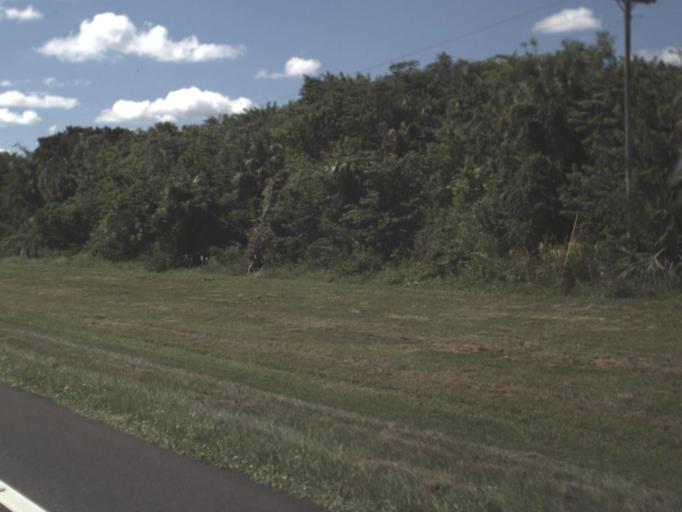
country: US
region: Florida
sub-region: Glades County
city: Buckhead Ridge
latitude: 27.0112
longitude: -81.0326
